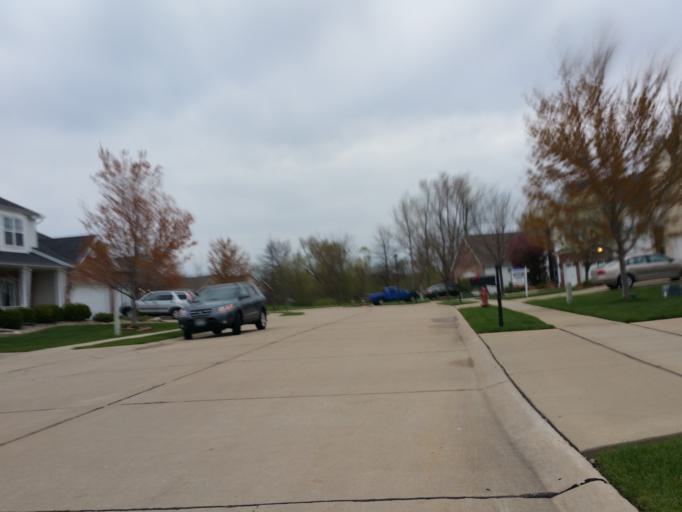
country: US
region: Illinois
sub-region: Madison County
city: Edwardsville
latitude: 38.7851
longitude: -89.9309
